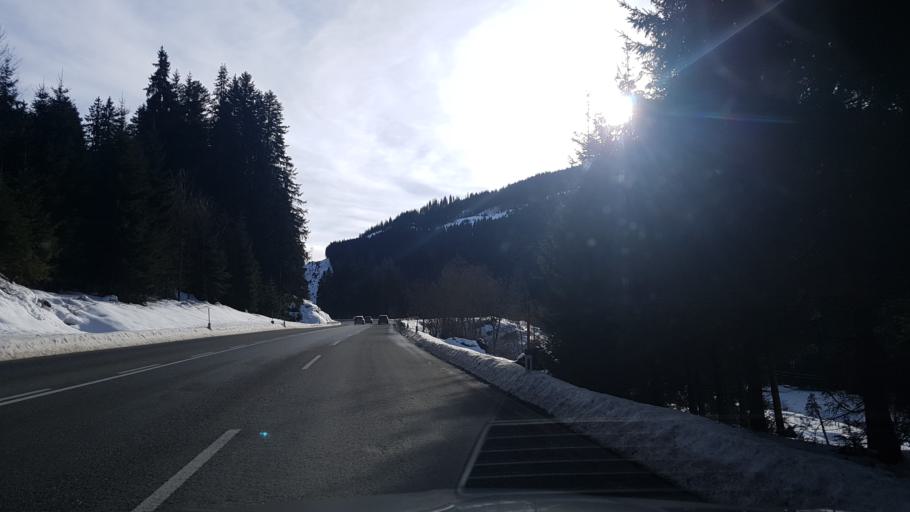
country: AT
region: Tyrol
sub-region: Politischer Bezirk Kitzbuhel
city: Jochberg
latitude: 47.3302
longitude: 12.4073
